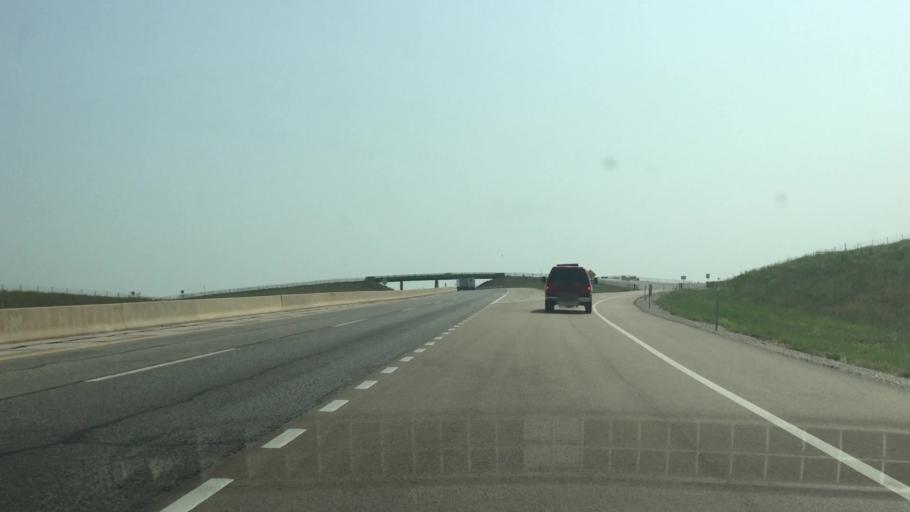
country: US
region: Kansas
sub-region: Chase County
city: Cottonwood Falls
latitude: 38.2285
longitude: -96.4130
